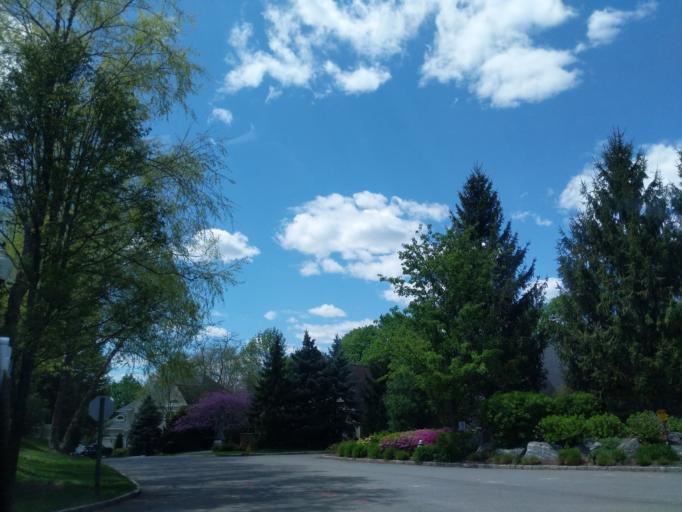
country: US
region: New York
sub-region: Westchester County
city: Tuckahoe
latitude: 40.9581
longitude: -73.7956
